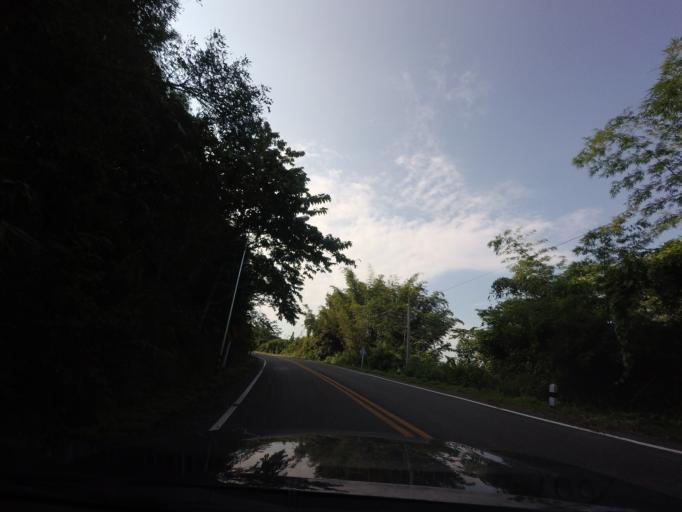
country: TH
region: Nan
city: Na Noi
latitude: 18.3681
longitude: 100.8331
